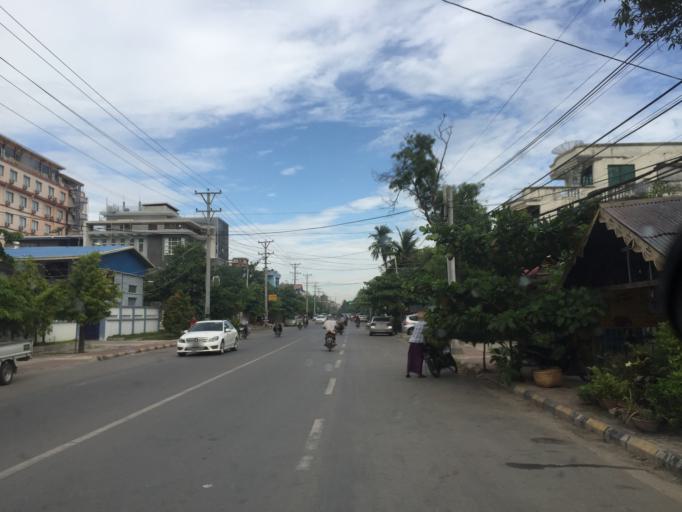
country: MM
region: Mandalay
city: Mandalay
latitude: 21.9728
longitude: 96.1053
